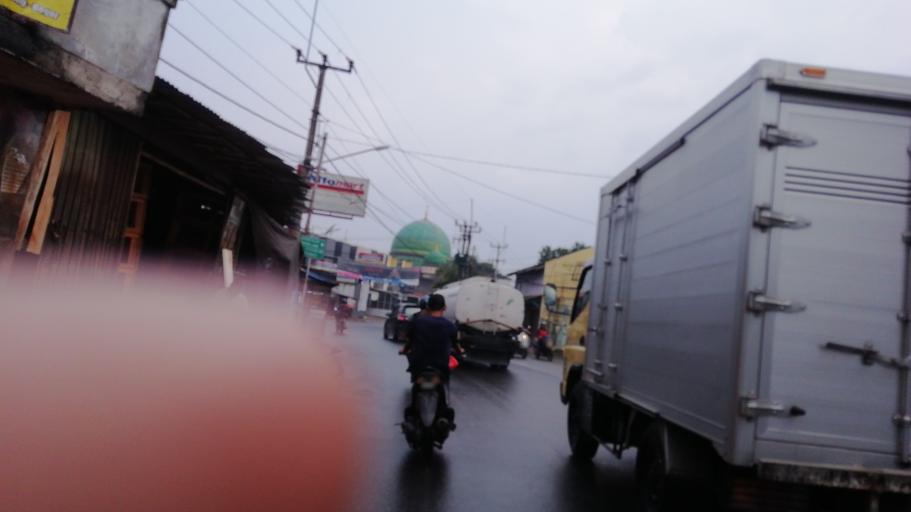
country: ID
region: West Java
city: Bogor
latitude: -6.5362
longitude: 106.8067
